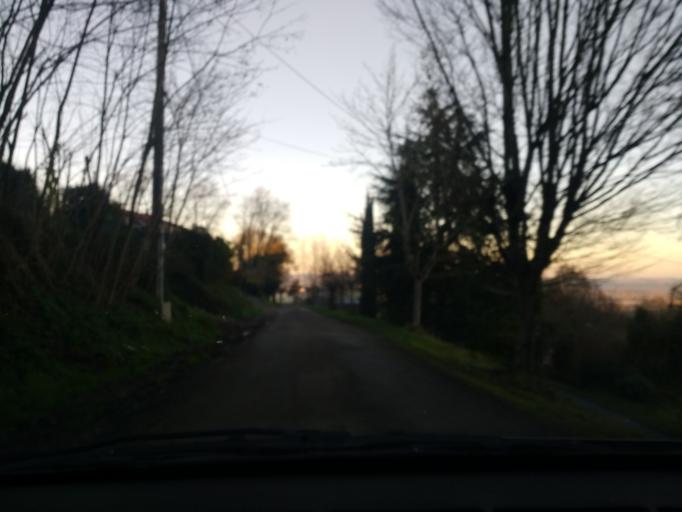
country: FR
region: Aquitaine
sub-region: Departement du Lot-et-Garonne
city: Castelmoron-sur-Lot
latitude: 44.3486
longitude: 0.5225
